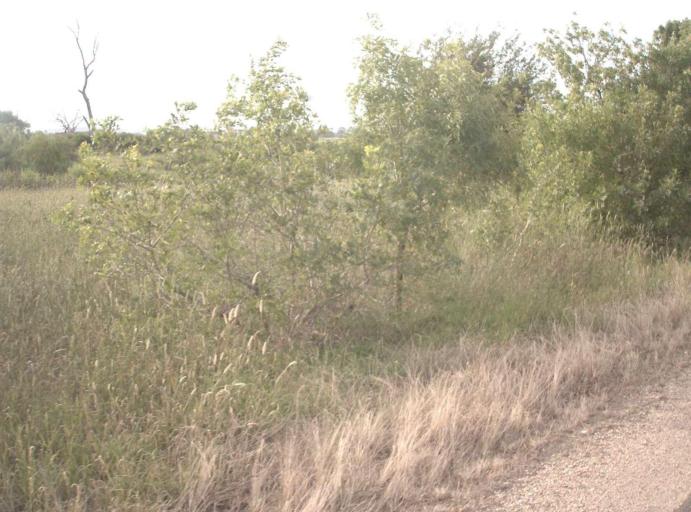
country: AU
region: Victoria
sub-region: Wellington
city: Heyfield
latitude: -37.9760
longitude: 146.8891
